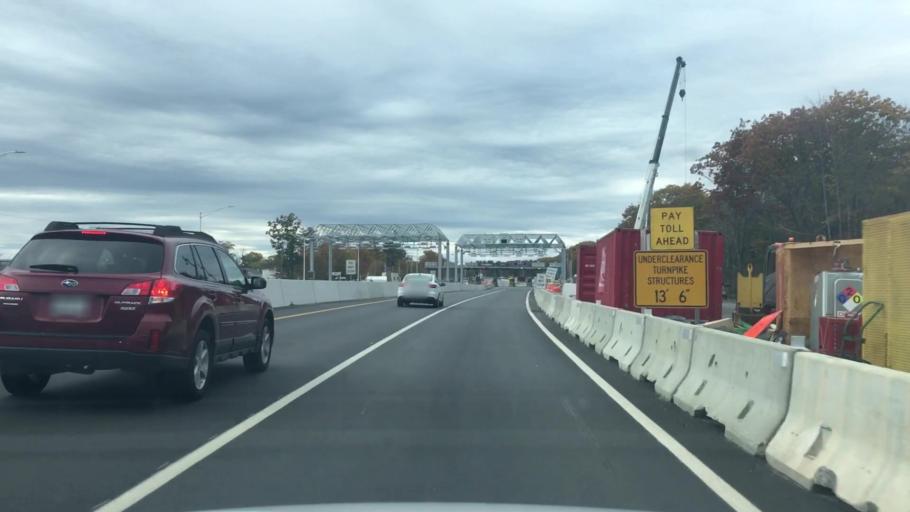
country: US
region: Maine
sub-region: Cumberland County
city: South Portland Gardens
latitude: 43.6257
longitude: -70.3395
